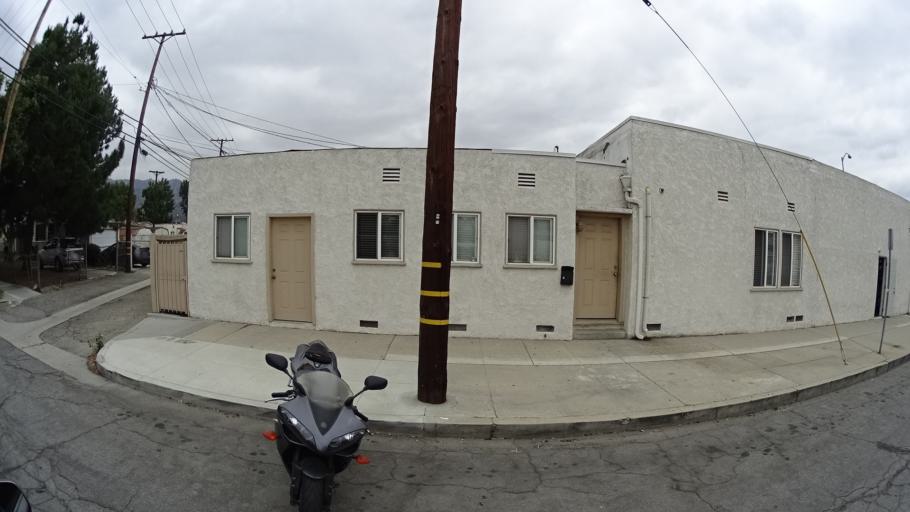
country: US
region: California
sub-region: Los Angeles County
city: Burbank
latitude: 34.1820
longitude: -118.3296
